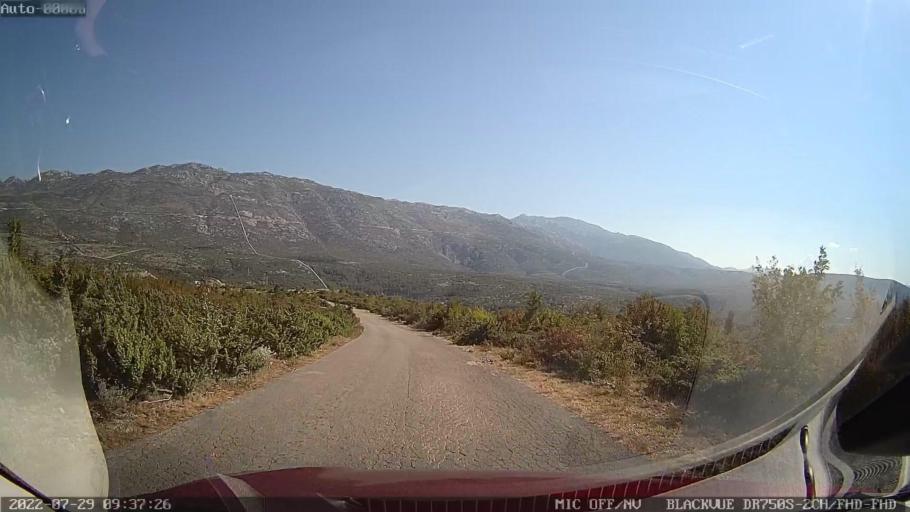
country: HR
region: Zadarska
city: Obrovac
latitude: 44.1960
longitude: 15.7453
